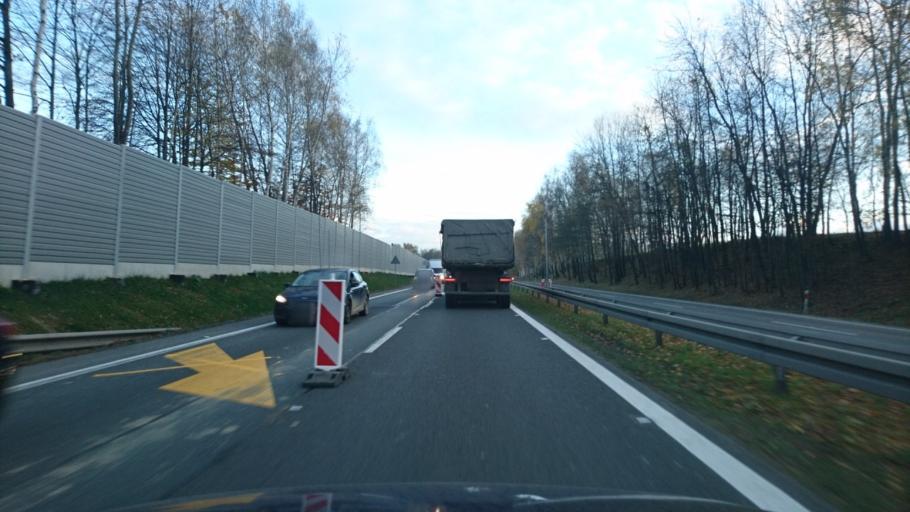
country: PL
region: Silesian Voivodeship
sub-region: Powiat bielski
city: Mazancowice
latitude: 49.8761
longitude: 18.9994
